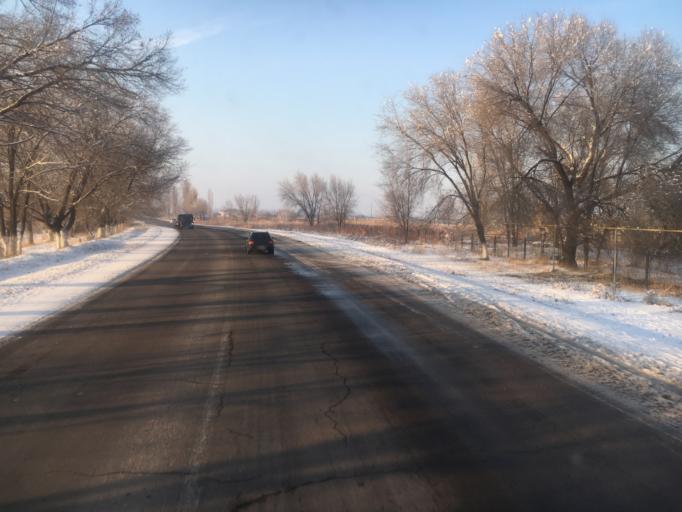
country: KZ
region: Almaty Oblysy
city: Burunday
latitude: 43.3408
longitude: 76.6585
